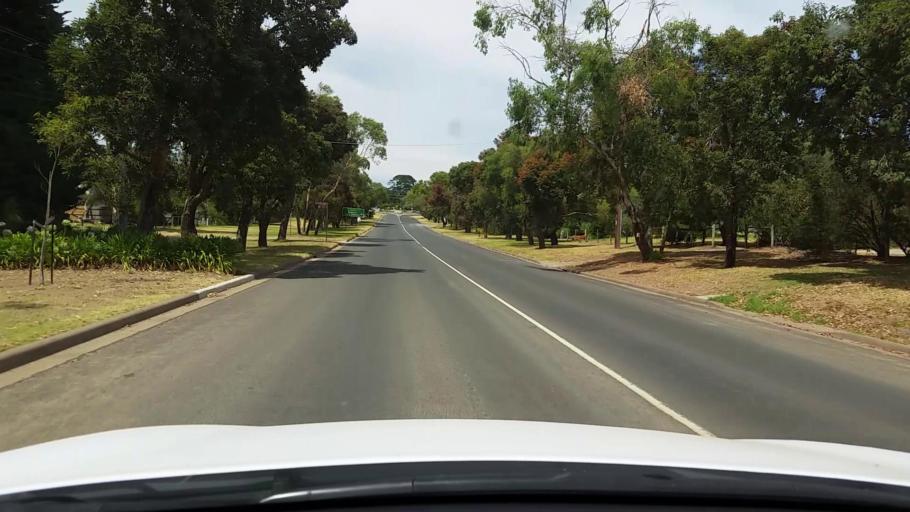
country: AU
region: Victoria
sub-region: Mornington Peninsula
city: Merricks
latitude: -38.4714
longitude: 145.0195
